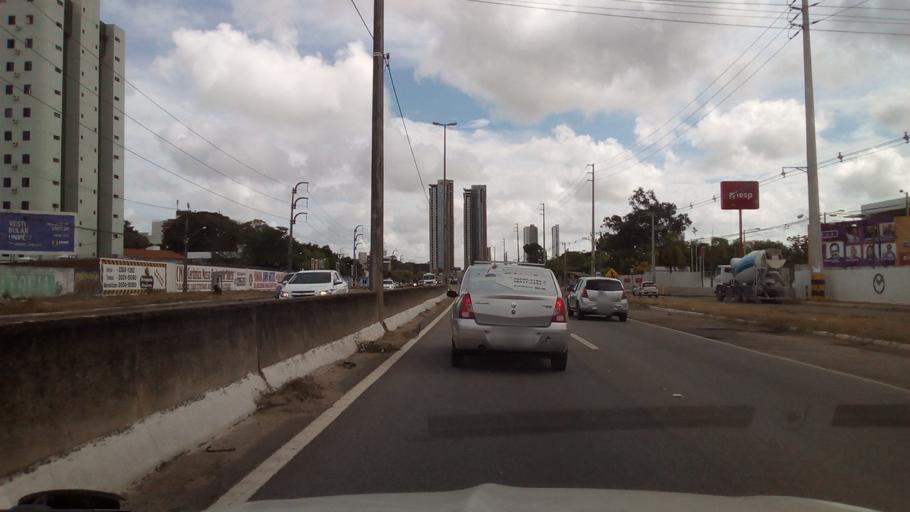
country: BR
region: Paraiba
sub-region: Joao Pessoa
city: Joao Pessoa
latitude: -7.0938
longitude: -34.8481
